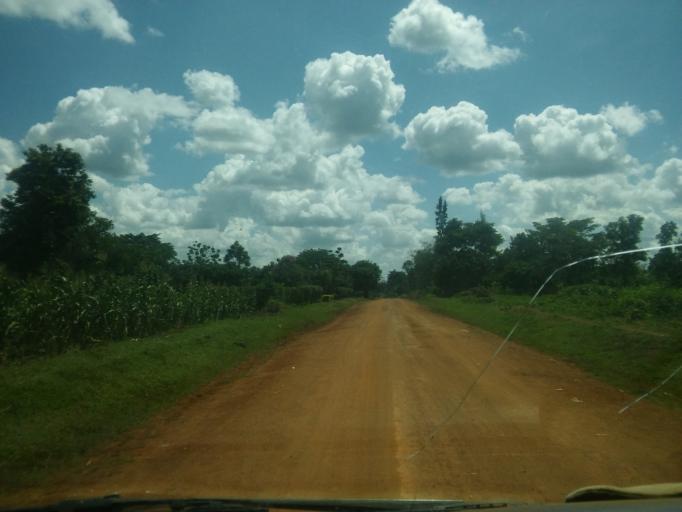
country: UG
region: Eastern Region
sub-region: Kibuku District
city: Kibuku
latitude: 1.1358
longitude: 33.8653
